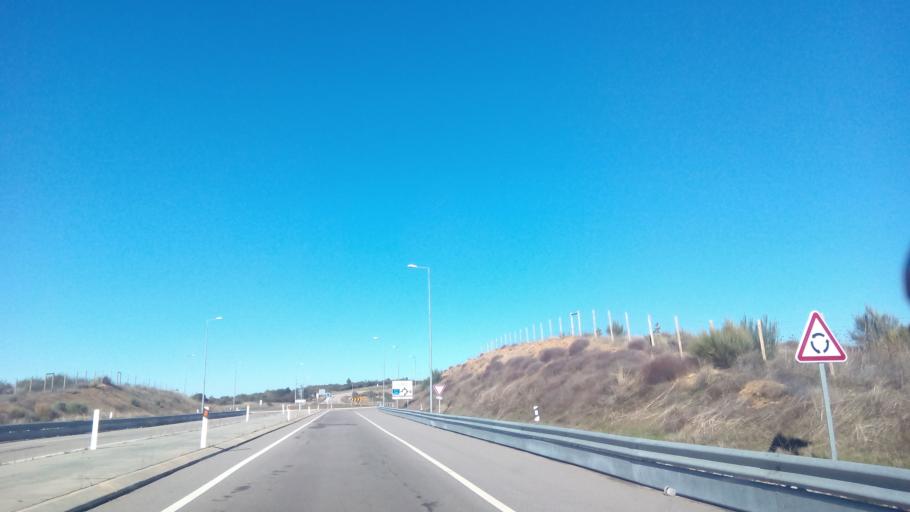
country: ES
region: Castille and Leon
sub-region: Provincia de Zamora
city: Trabazos
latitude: 41.7446
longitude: -6.6213
